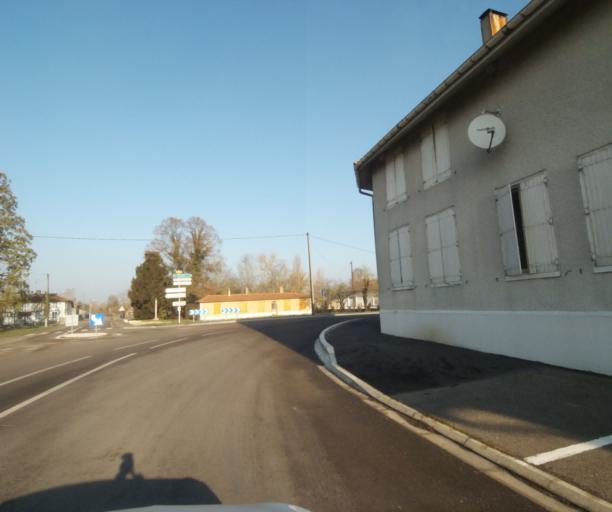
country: FR
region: Champagne-Ardenne
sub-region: Departement de la Haute-Marne
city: Montier-en-Der
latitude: 48.4731
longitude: 4.7646
